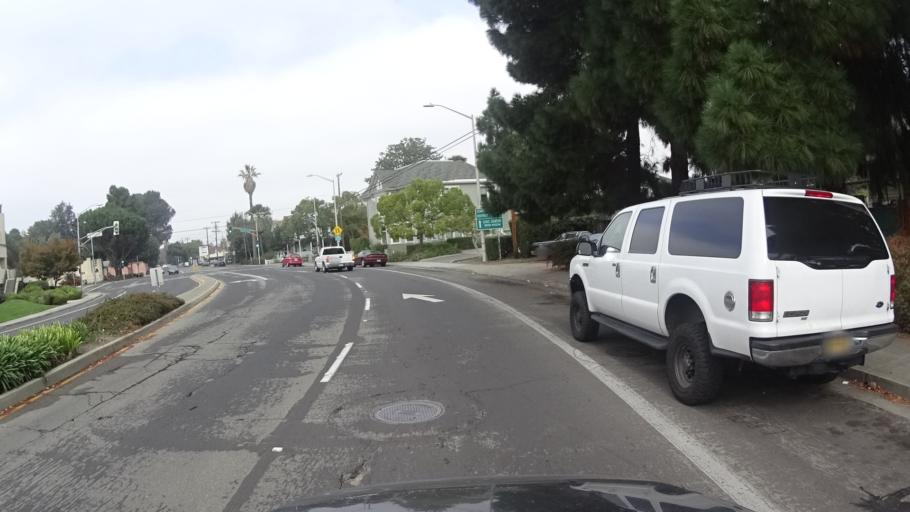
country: US
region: California
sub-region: Santa Clara County
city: Santa Clara
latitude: 37.3456
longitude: -121.9509
